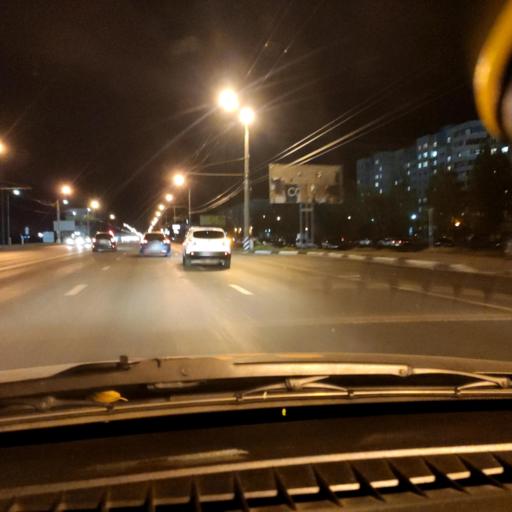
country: RU
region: Samara
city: Tol'yatti
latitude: 53.5484
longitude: 49.3433
